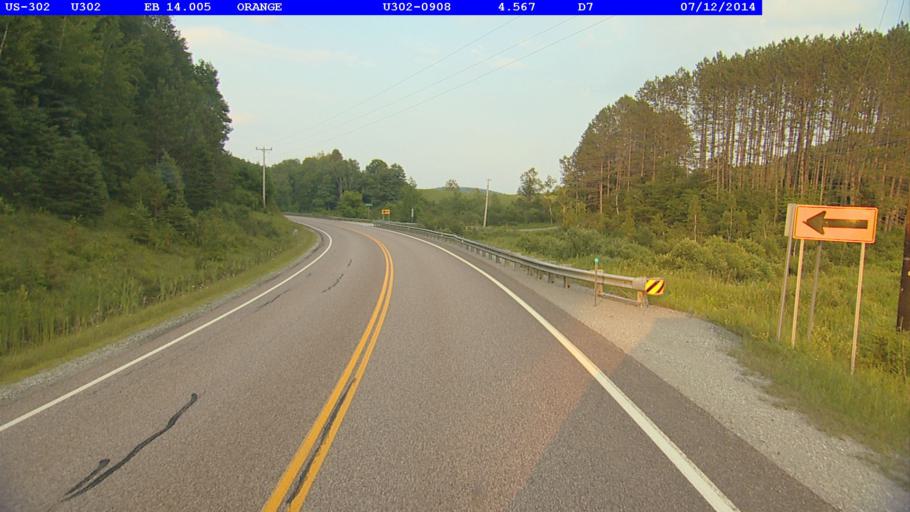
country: US
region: Vermont
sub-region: Washington County
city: South Barre
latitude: 44.1416
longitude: -72.3494
